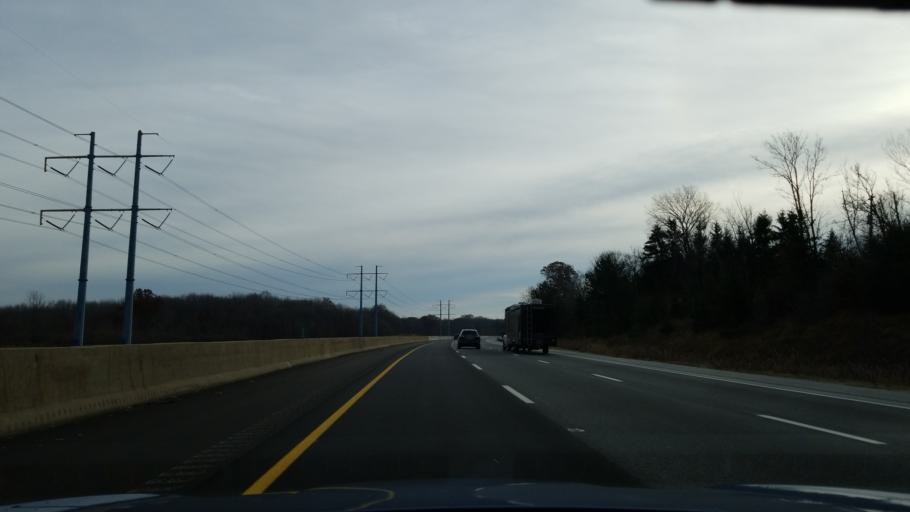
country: US
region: Ohio
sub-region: Cuyahoga County
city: North Royalton
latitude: 41.3027
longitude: -81.7084
